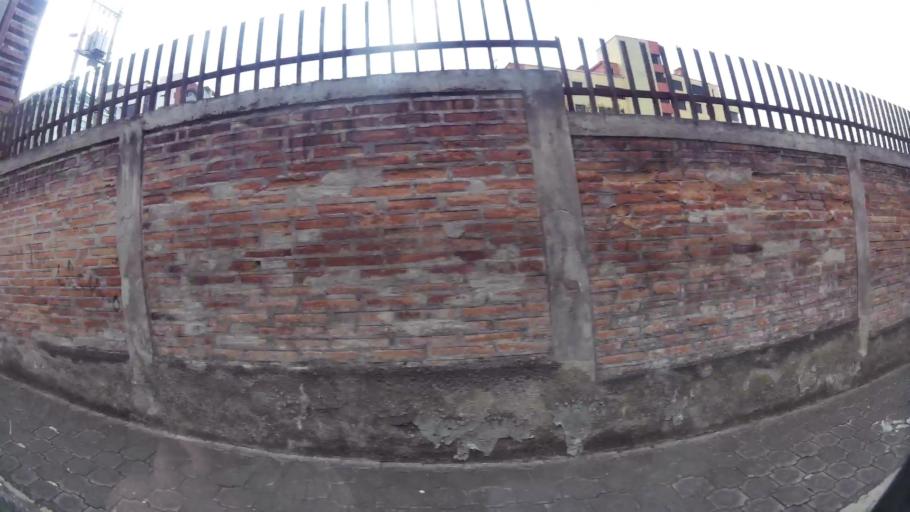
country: EC
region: Pichincha
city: Quito
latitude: -0.1655
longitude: -78.4956
